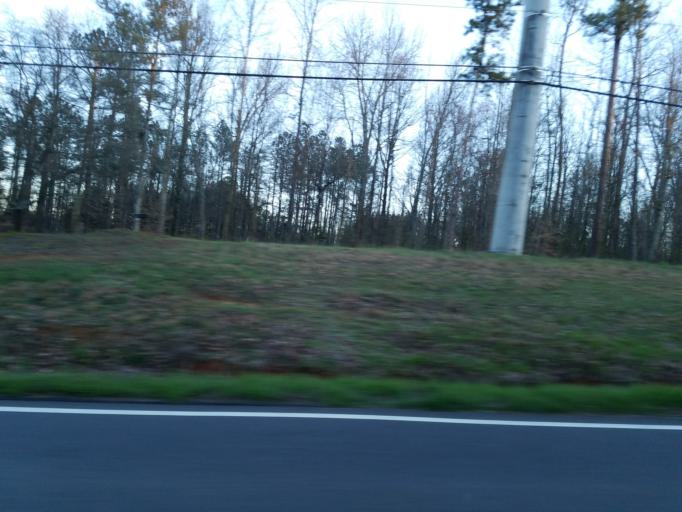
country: US
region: Georgia
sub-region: Hall County
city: Oakwood
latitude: 34.2975
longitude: -83.9903
